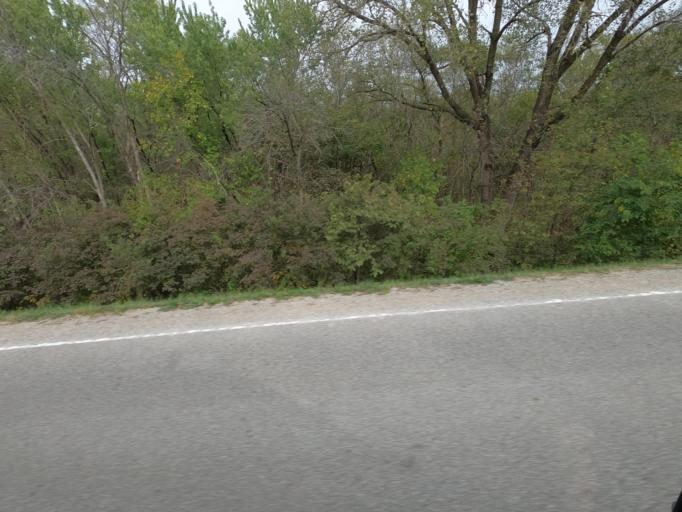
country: US
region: Iowa
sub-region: Jefferson County
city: Fairfield
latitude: 40.8795
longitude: -92.1581
